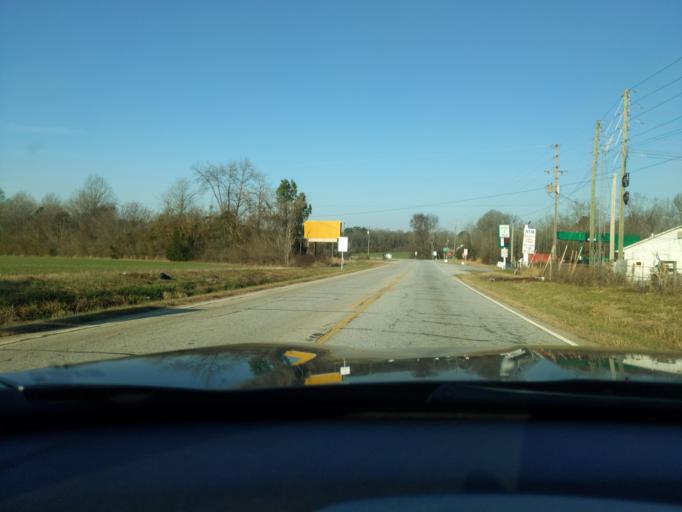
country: US
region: South Carolina
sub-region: Newberry County
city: Newberry
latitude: 34.2233
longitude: -81.7287
